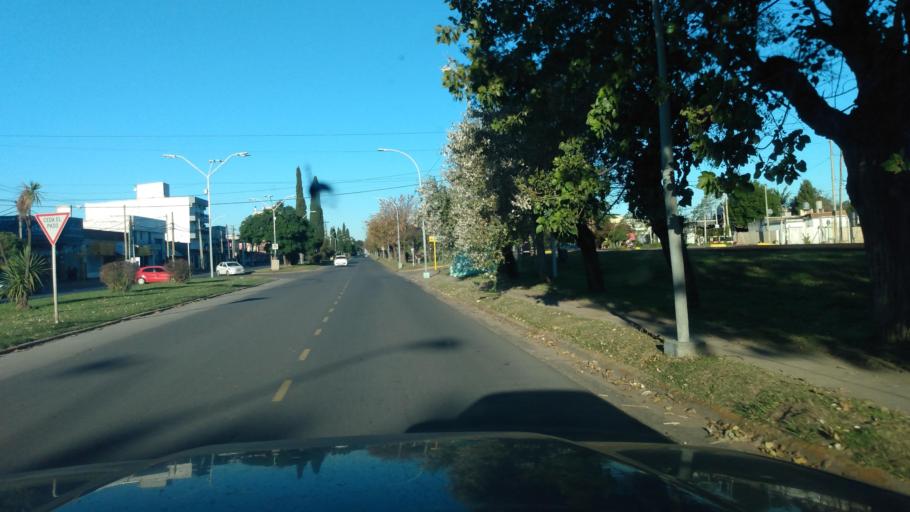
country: AR
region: Buenos Aires
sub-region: Partido de General Rodriguez
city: General Rodriguez
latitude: -34.6095
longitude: -58.9492
